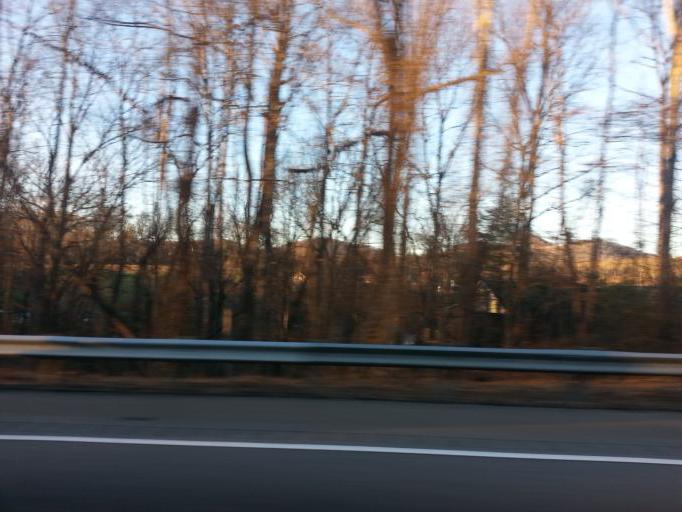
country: US
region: North Carolina
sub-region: Buncombe County
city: Bent Creek
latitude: 35.5545
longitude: -82.6759
